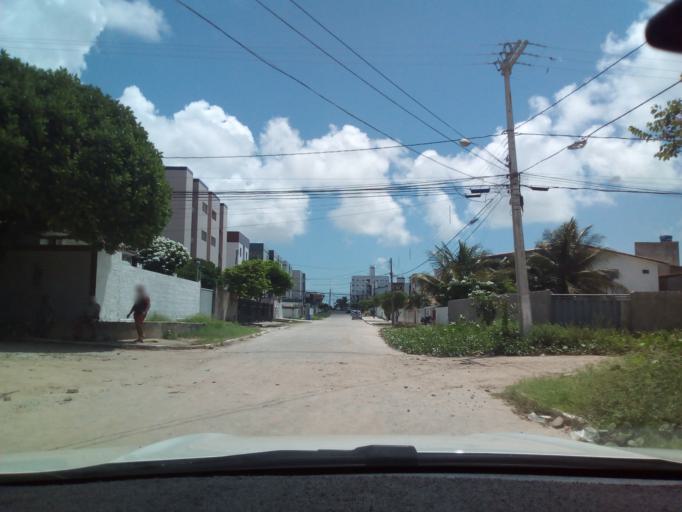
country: BR
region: Paraiba
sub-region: Joao Pessoa
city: Joao Pessoa
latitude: -7.1554
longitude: -34.8318
